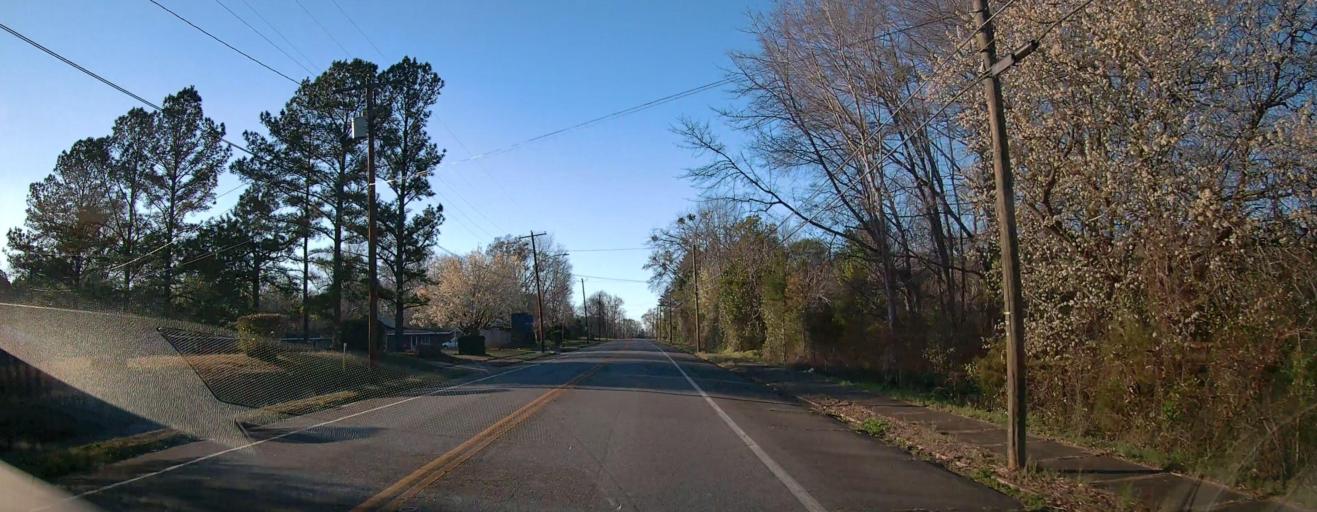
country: US
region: Georgia
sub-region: Talbot County
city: Talbotton
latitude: 32.6703
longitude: -84.5360
